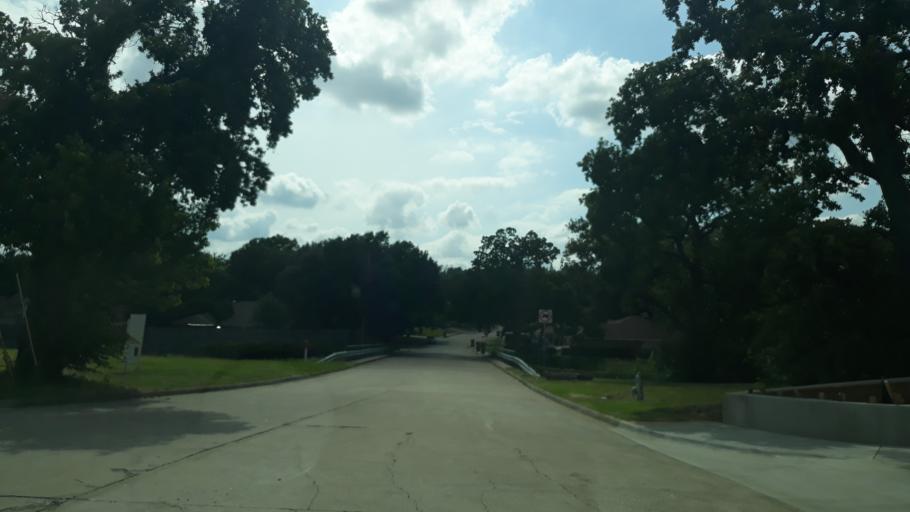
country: US
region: Texas
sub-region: Dallas County
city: Irving
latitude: 32.8128
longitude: -96.9945
